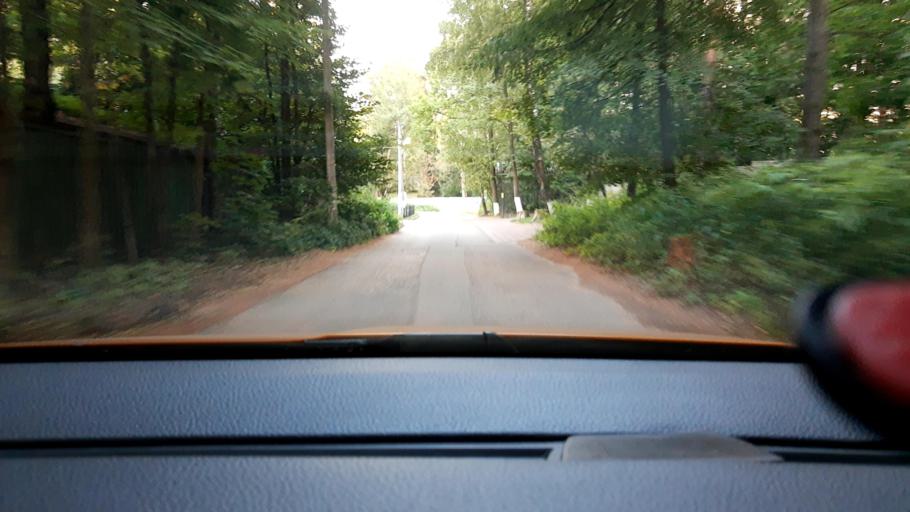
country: RU
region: Moscow
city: Novo-Peredelkino
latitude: 55.6660
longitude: 37.3408
